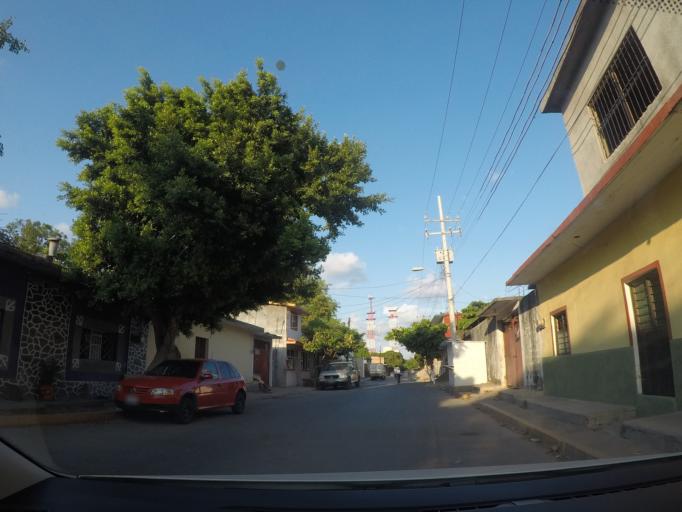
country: MX
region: Oaxaca
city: Juchitan de Zaragoza
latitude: 16.4424
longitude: -95.0242
